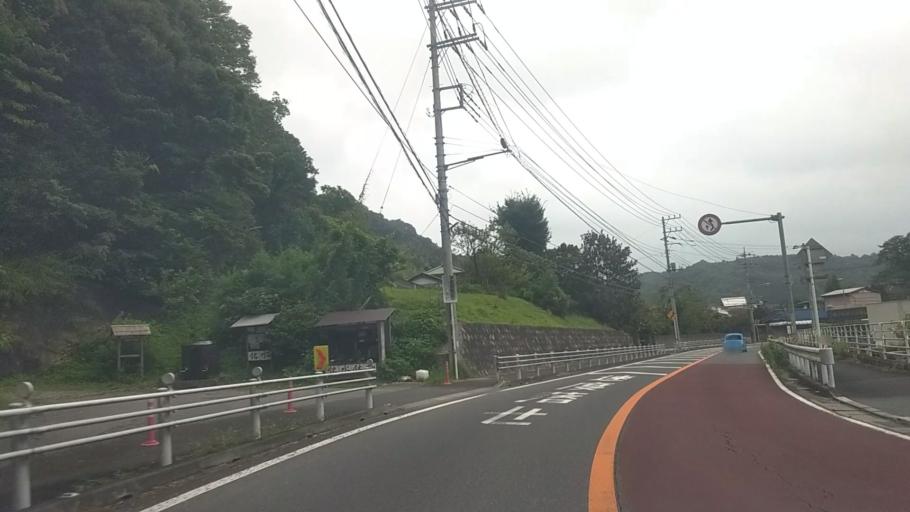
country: JP
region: Chiba
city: Kisarazu
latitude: 35.2917
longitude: 140.0833
